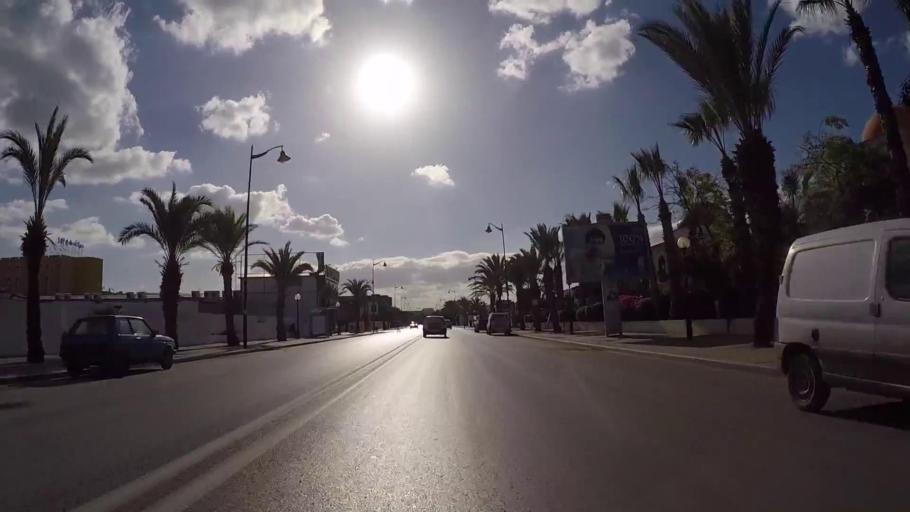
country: TN
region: Nabul
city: Al Hammamat
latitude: 36.3679
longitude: 10.5352
